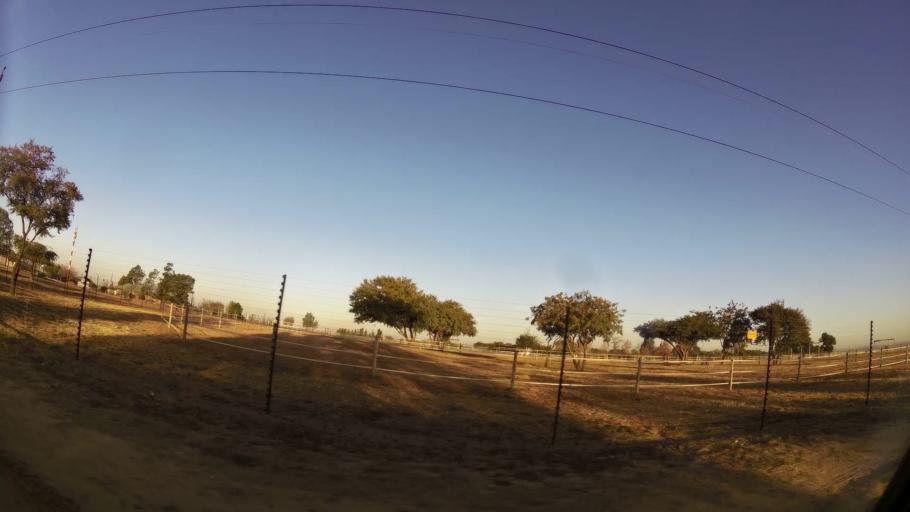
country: ZA
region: Gauteng
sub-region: City of Johannesburg Metropolitan Municipality
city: Diepsloot
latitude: -25.9333
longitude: 28.0513
